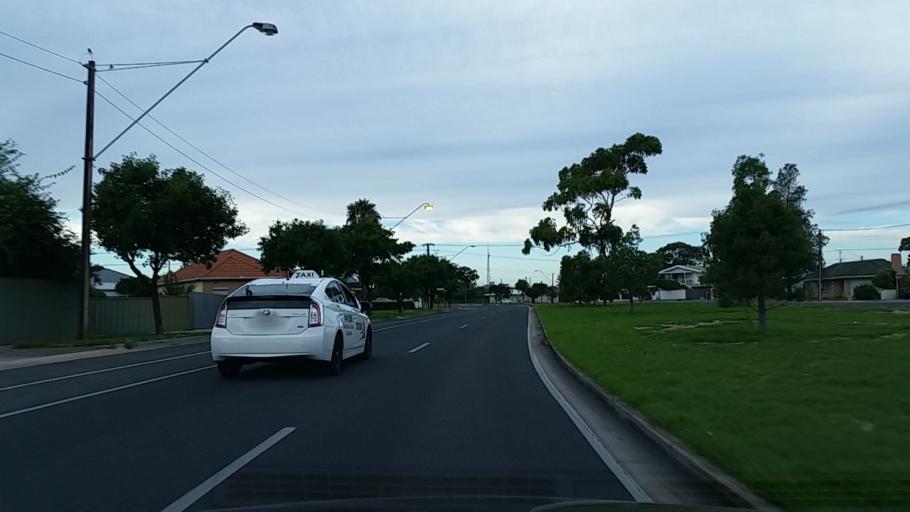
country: AU
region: South Australia
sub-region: City of West Torrens
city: Plympton
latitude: -34.9277
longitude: 138.5438
